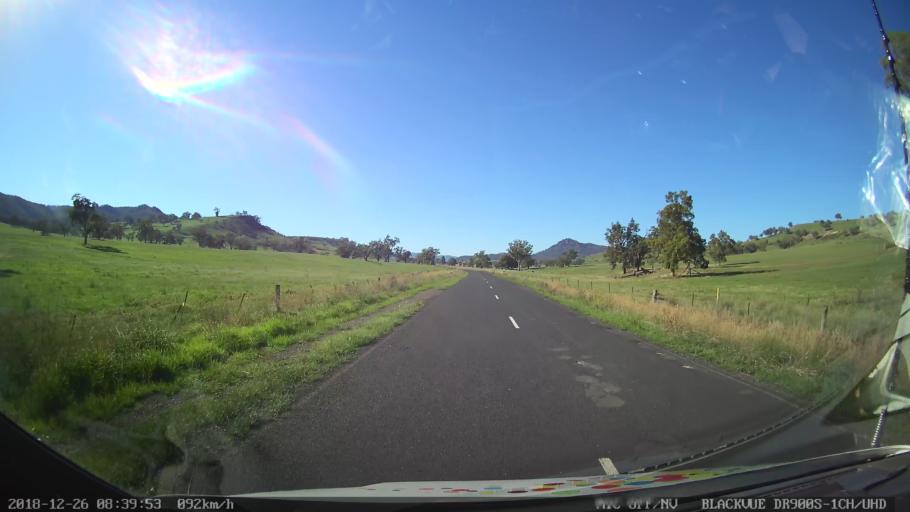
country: AU
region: New South Wales
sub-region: Mid-Western Regional
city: Kandos
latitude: -32.4595
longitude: 150.0756
